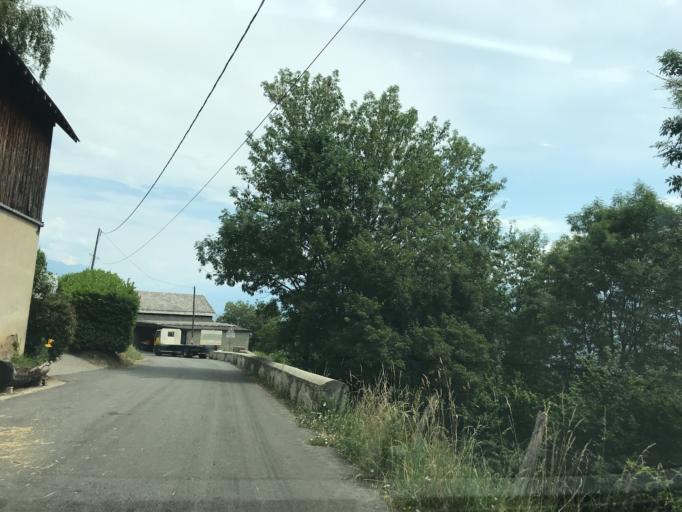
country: FR
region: Rhone-Alpes
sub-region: Departement de l'Isere
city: Barraux
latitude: 45.4507
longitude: 5.9643
